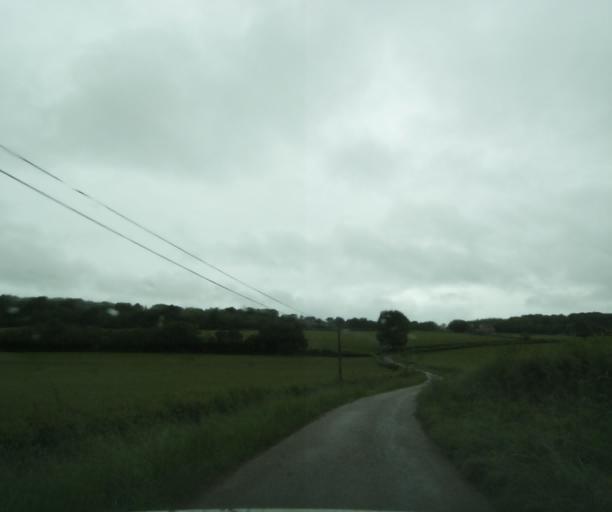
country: FR
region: Bourgogne
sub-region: Departement de Saone-et-Loire
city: Charolles
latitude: 46.4868
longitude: 4.2910
